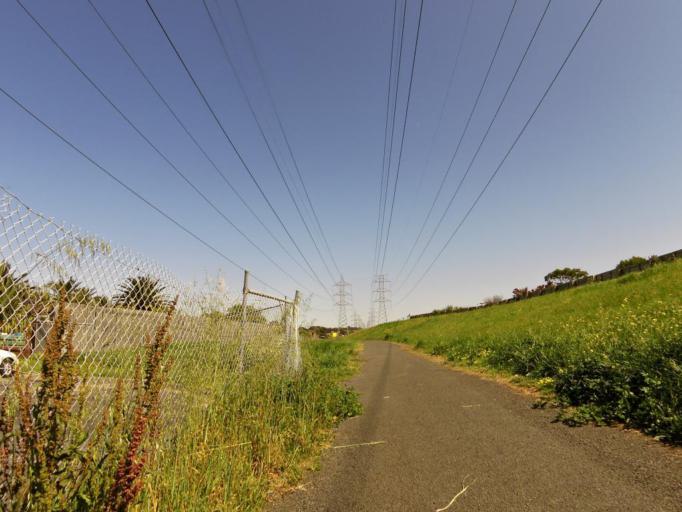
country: AU
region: Victoria
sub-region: Hume
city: Campbellfield
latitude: -37.6920
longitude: 144.9647
